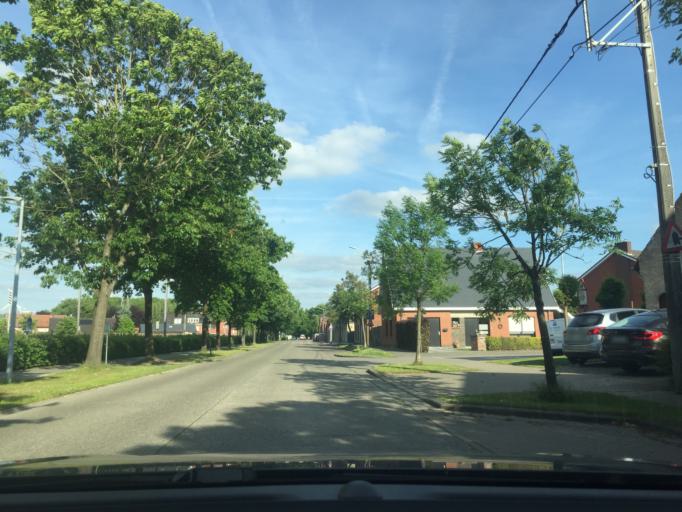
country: BE
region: Flanders
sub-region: Provincie West-Vlaanderen
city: Roeselare
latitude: 50.9404
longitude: 3.1404
